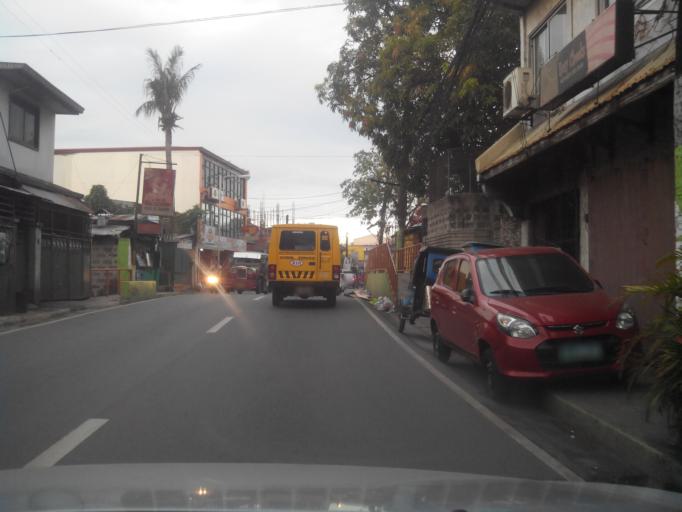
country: PH
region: Calabarzon
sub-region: Province of Rizal
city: Cainta
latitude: 14.5717
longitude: 121.1285
